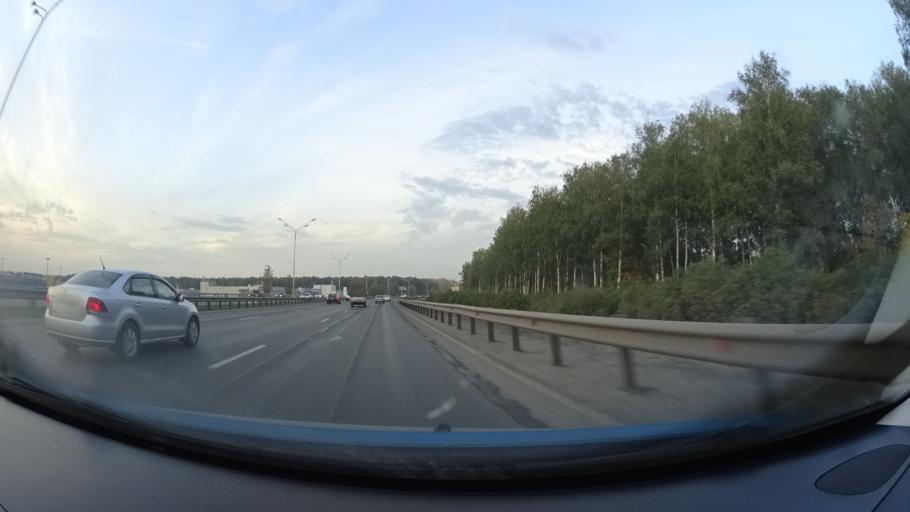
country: RU
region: Bashkortostan
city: Ufa
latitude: 54.6787
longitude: 55.9337
